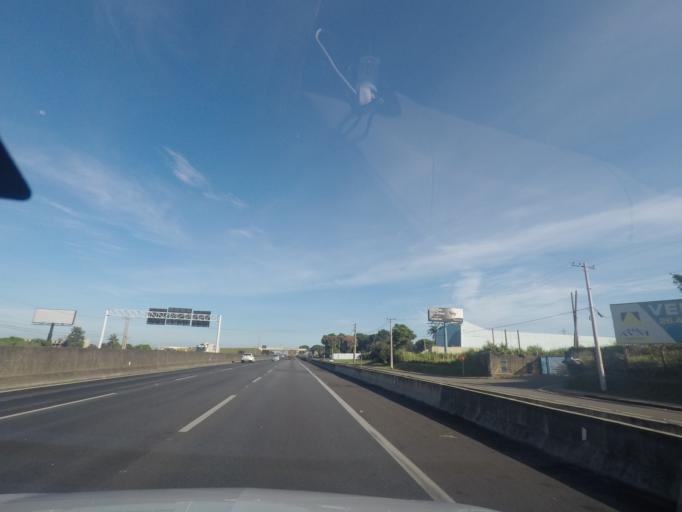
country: BR
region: Sao Paulo
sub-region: Nova Odessa
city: Nova Odessa
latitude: -22.7570
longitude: -47.2544
